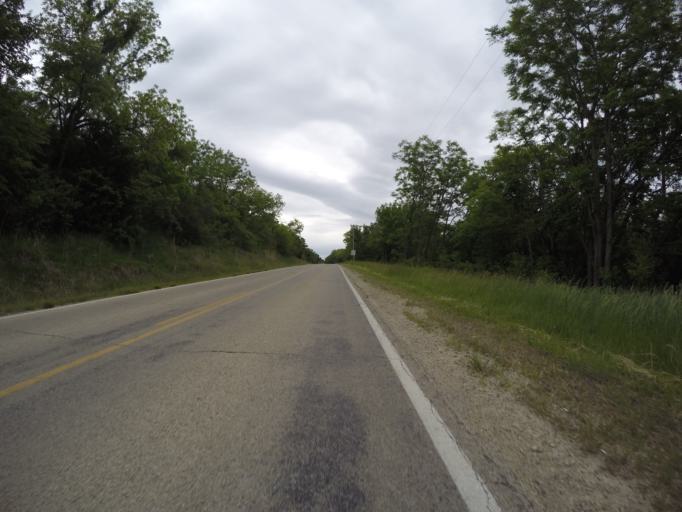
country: US
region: Kansas
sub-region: Pottawatomie County
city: Wamego
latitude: 39.1823
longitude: -96.3686
